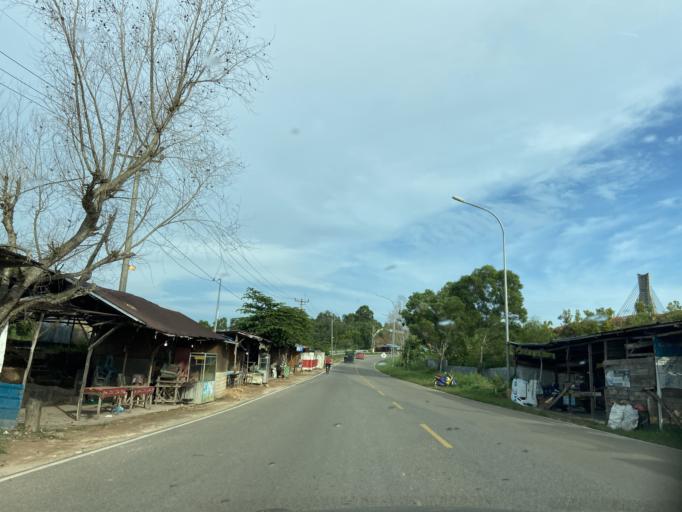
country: SG
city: Singapore
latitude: 0.9769
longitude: 104.0464
